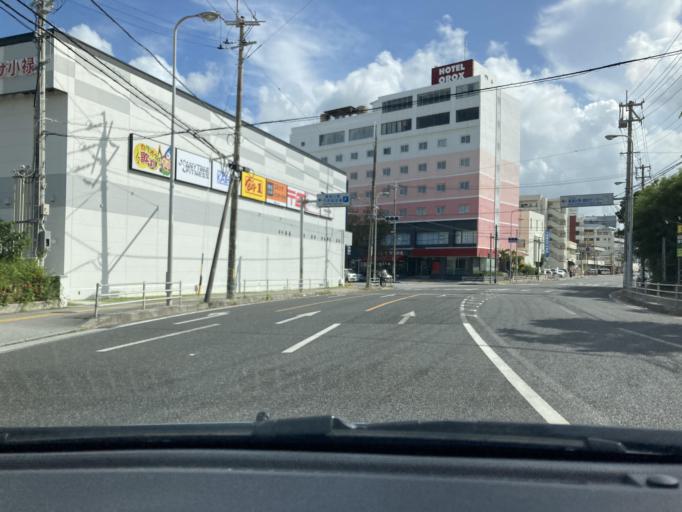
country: JP
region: Okinawa
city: Tomigusuku
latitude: 26.1969
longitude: 127.6763
